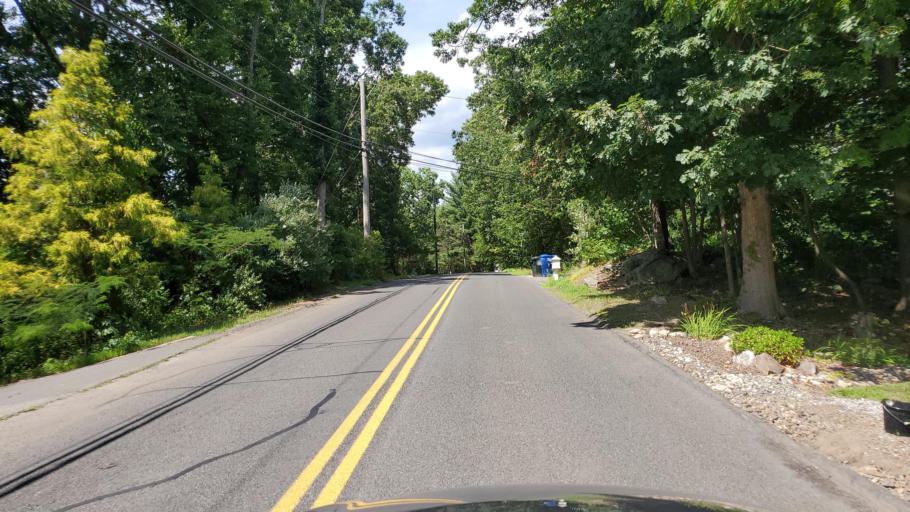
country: US
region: Connecticut
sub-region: Fairfield County
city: Newtown
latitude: 41.3411
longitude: -73.2787
